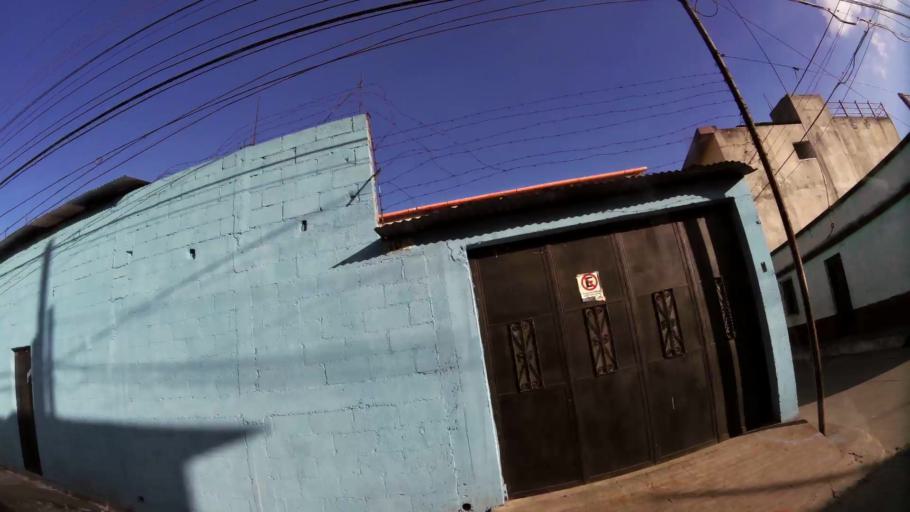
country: GT
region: Guatemala
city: Villa Nueva
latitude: 14.5175
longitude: -90.5862
